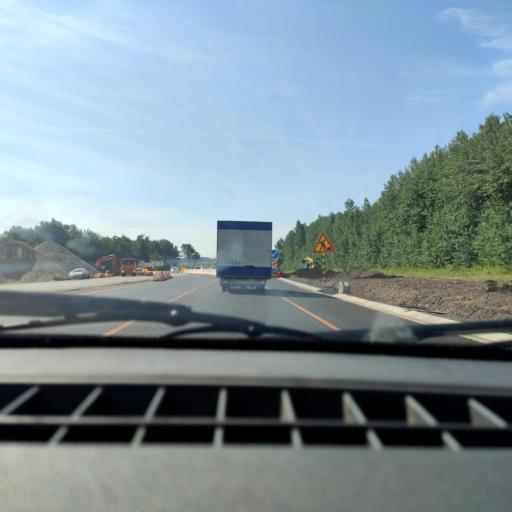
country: RU
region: Bashkortostan
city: Tolbazy
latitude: 54.1179
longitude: 55.9007
